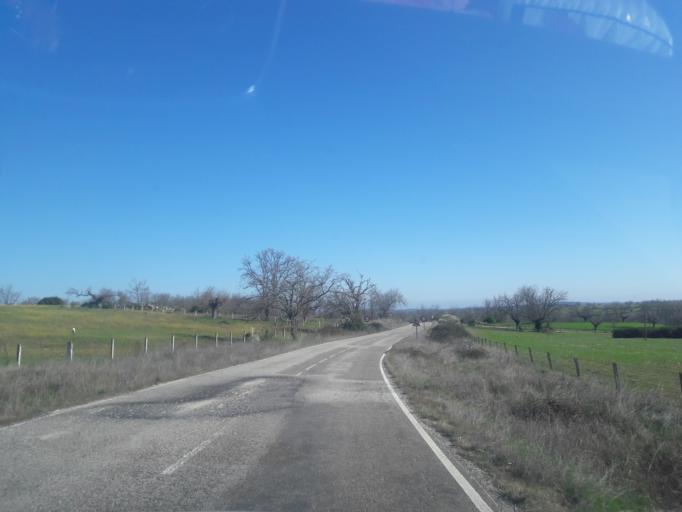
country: ES
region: Castille and Leon
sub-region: Provincia de Salamanca
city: Cabeza del Caballo
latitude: 41.1420
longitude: -6.5578
